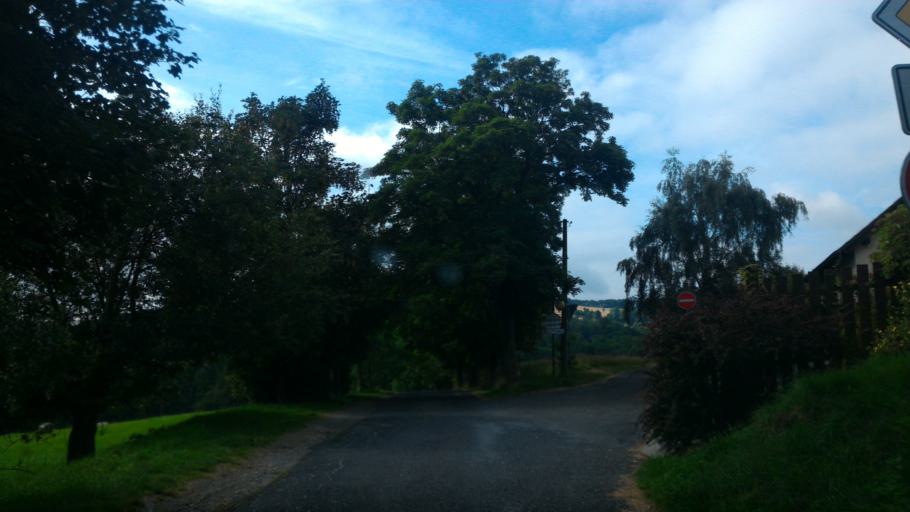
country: CZ
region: Ustecky
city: Dolni Podluzi
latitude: 50.8703
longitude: 14.5764
